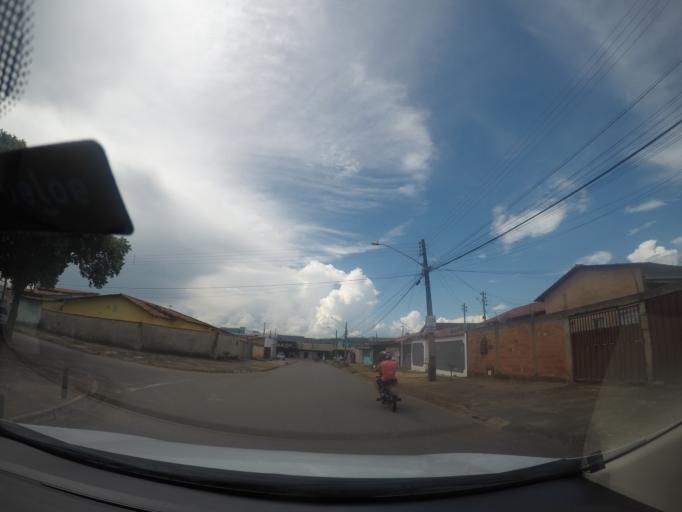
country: BR
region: Goias
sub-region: Goiania
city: Goiania
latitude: -16.6967
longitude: -49.3560
